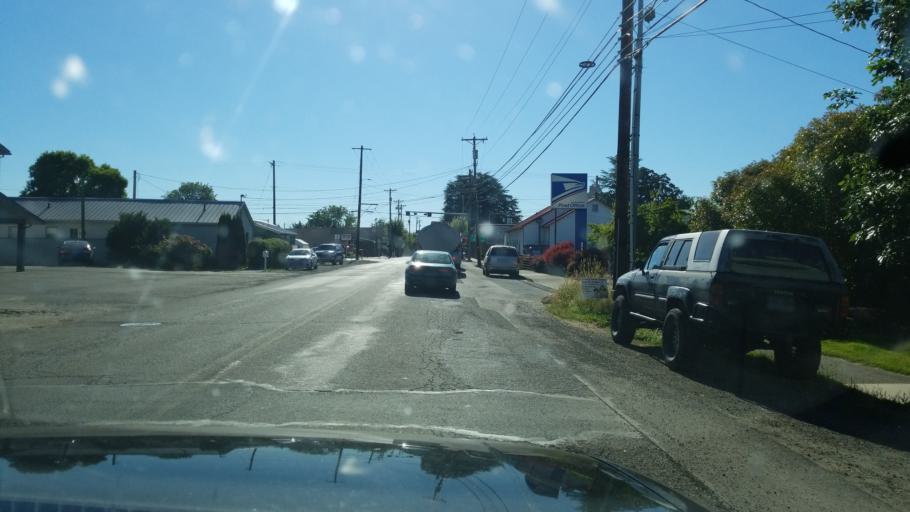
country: US
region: Oregon
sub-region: Yamhill County
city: Carlton
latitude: 45.2942
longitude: -123.1809
